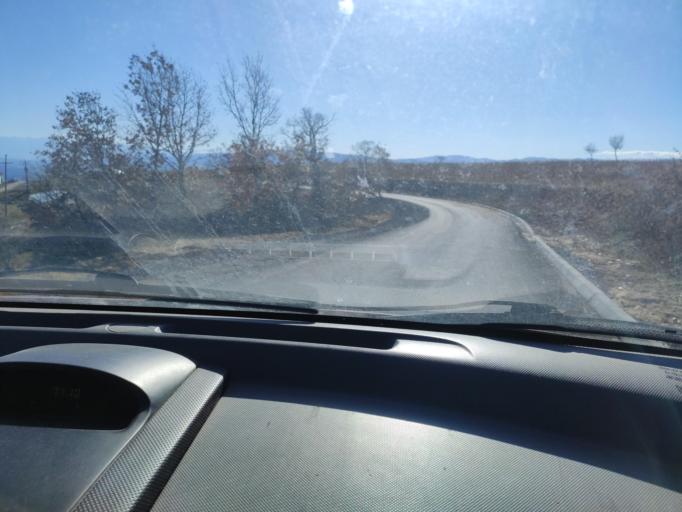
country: MK
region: Radovis
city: Radovish
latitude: 41.6621
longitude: 22.4098
